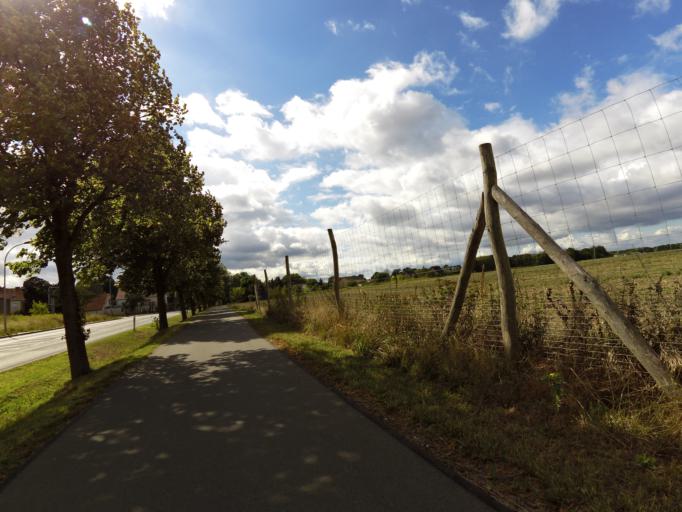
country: DE
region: Berlin
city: Lichtenrade
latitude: 52.3666
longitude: 13.3961
